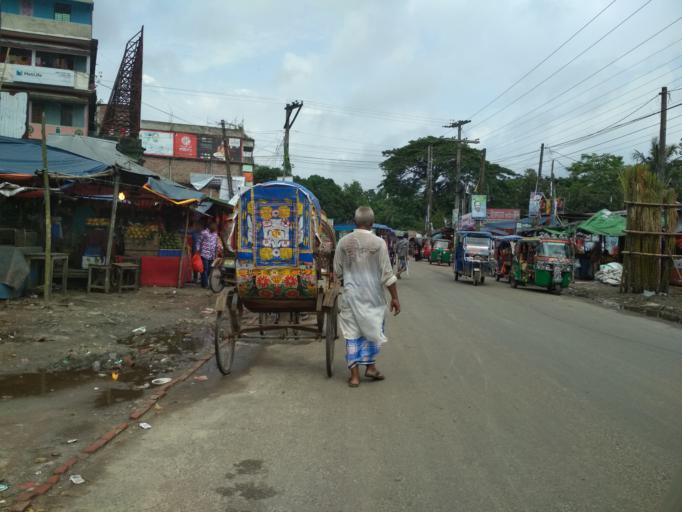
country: BD
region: Chittagong
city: Lakshmipur
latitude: 22.9694
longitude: 90.8063
